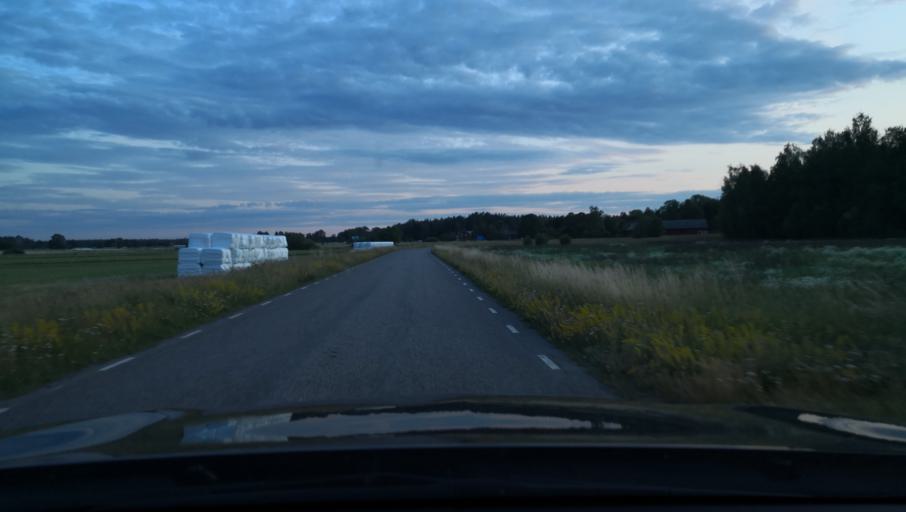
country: SE
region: Uppsala
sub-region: Osthammars Kommun
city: Bjorklinge
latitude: 60.0478
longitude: 17.5054
